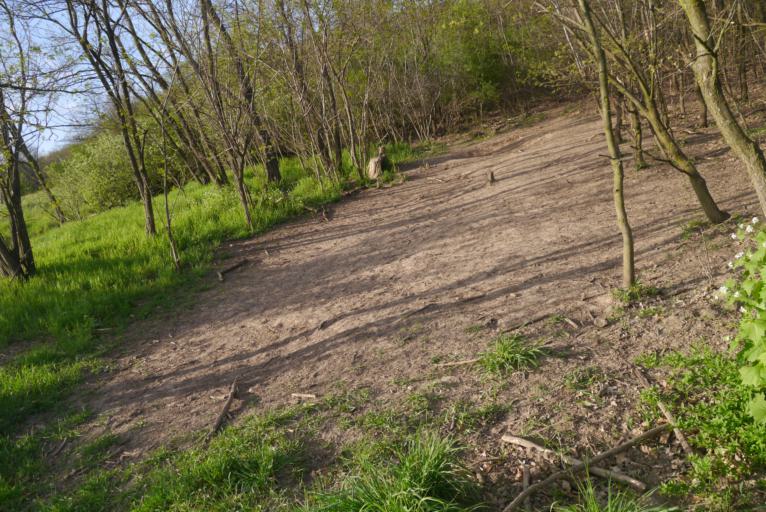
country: HU
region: Pest
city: Piliscsaba
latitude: 47.6538
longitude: 18.8214
